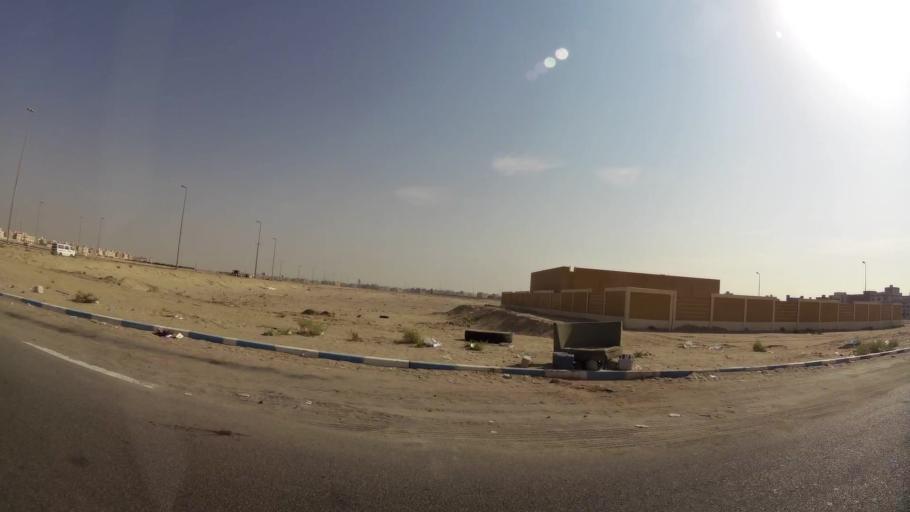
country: KW
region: Al Ahmadi
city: Al Wafrah
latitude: 28.7824
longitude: 48.0686
